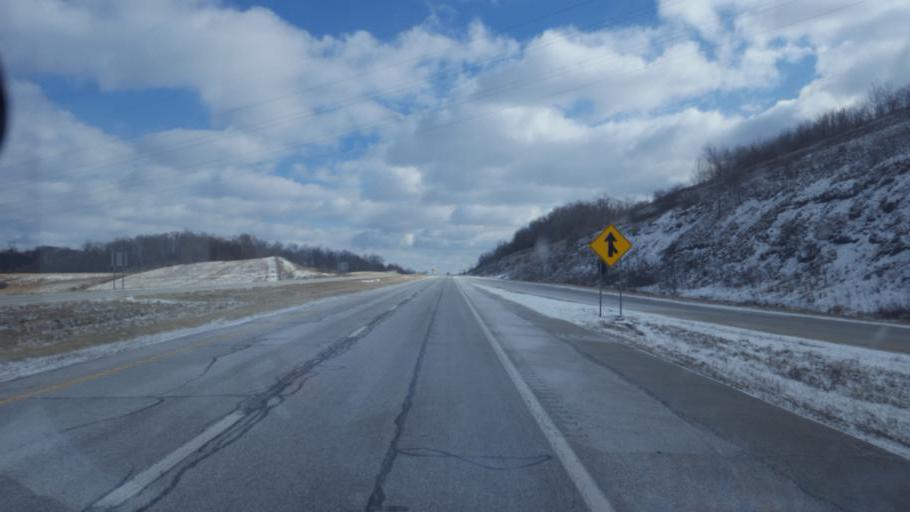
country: US
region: Ohio
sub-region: Muskingum County
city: Dresden
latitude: 40.1547
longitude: -82.0208
